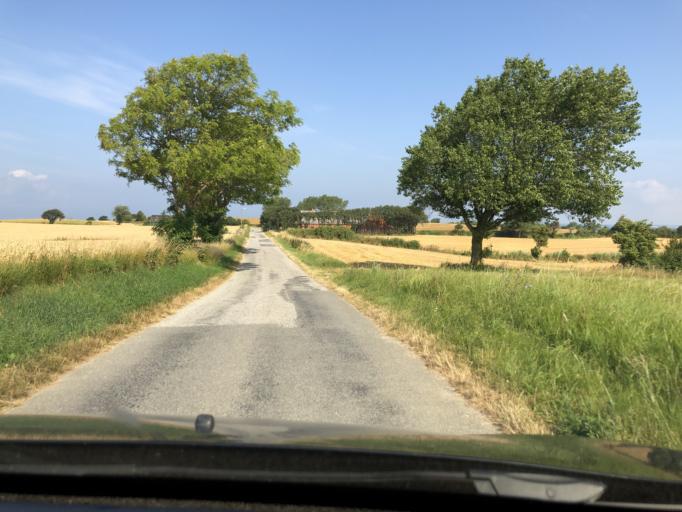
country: DK
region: South Denmark
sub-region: Faaborg-Midtfyn Kommune
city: Faaborg
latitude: 54.9600
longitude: 10.2191
